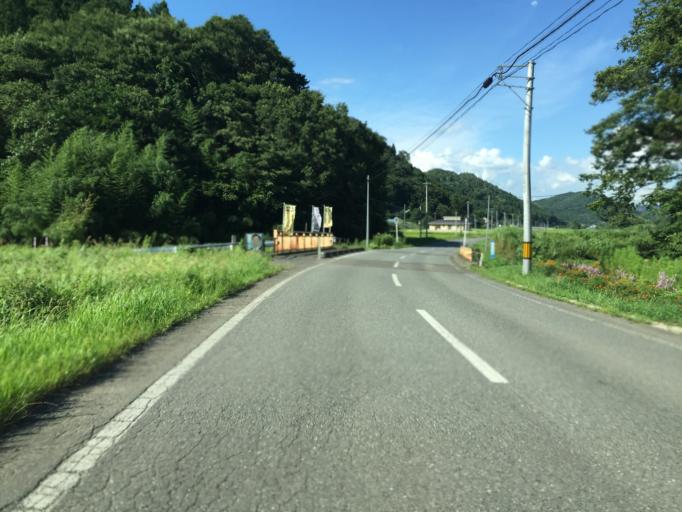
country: JP
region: Fukushima
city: Hobaramachi
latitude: 37.7505
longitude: 140.5662
